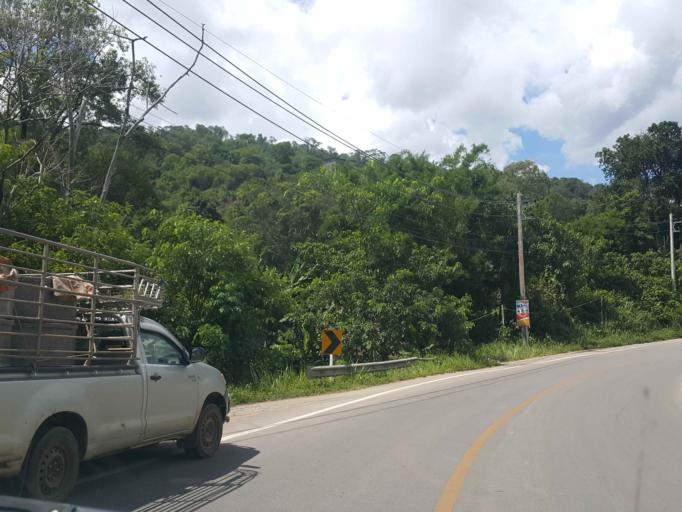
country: TH
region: Chiang Mai
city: Samoeng
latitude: 18.8838
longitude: 98.8144
